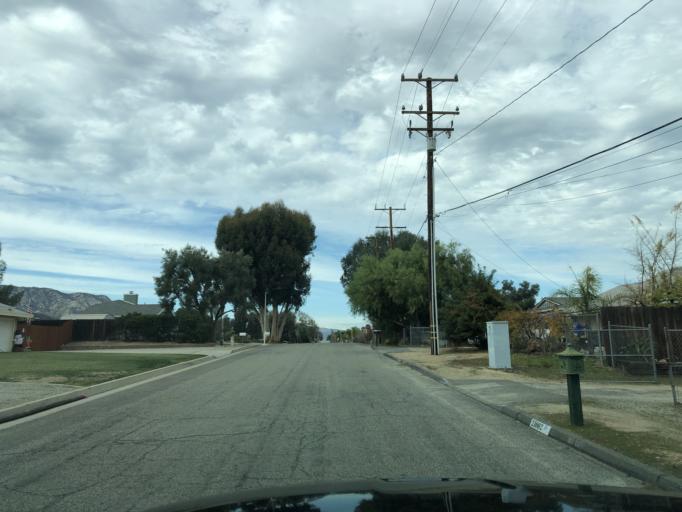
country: US
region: California
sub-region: Riverside County
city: Wildomar
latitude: 33.6069
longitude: -117.2853
